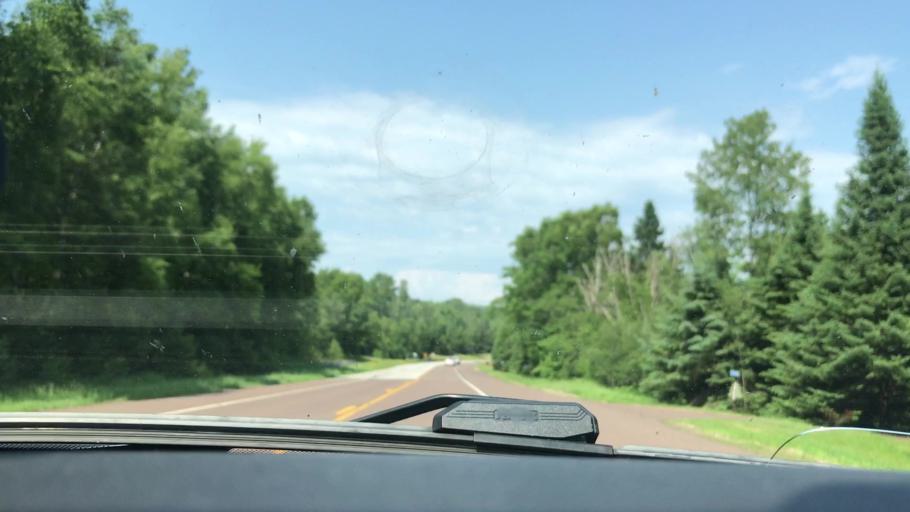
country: US
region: Minnesota
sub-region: Cook County
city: Grand Marais
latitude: 47.7820
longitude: -90.1864
